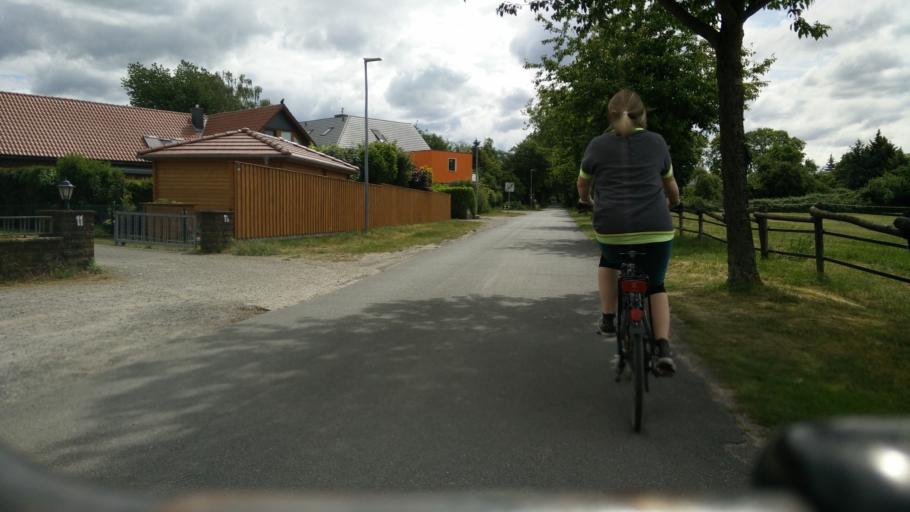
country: DE
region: Lower Saxony
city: Hagenburg
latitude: 52.4512
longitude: 9.3626
